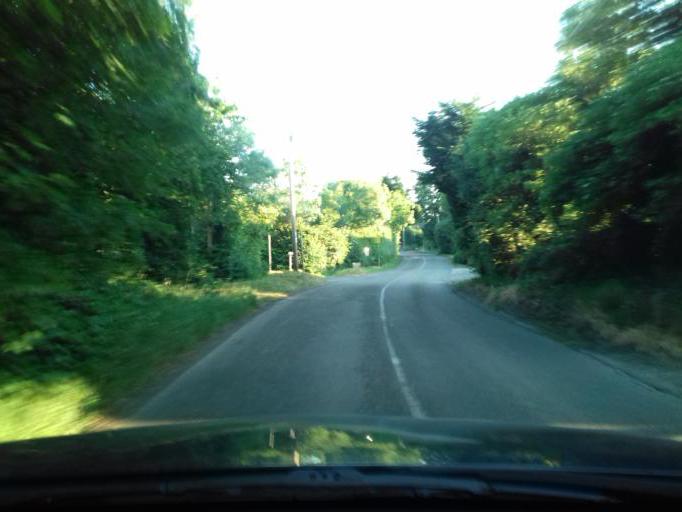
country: IE
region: Leinster
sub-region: An Mhi
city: Ashbourne
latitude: 53.4773
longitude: -6.3172
